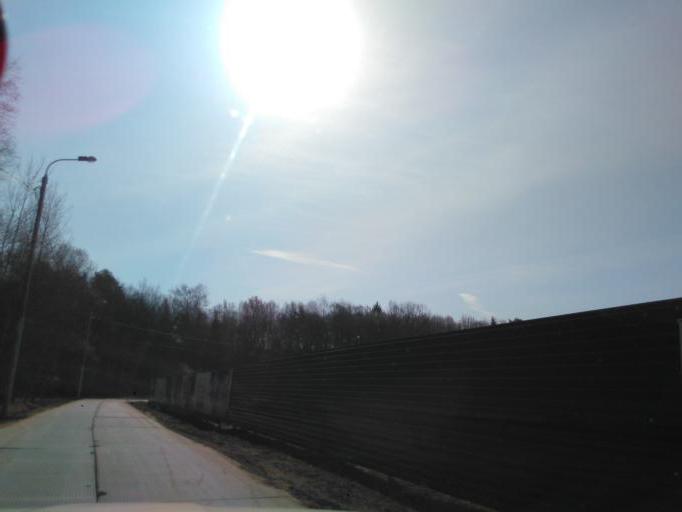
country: RU
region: Moskovskaya
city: Opalikha
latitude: 55.8741
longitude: 37.2606
